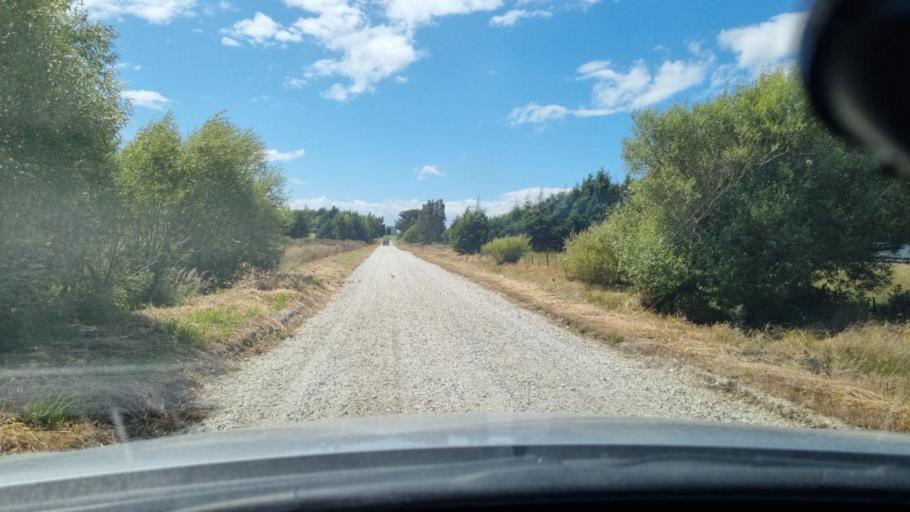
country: NZ
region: Southland
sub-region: Invercargill City
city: Invercargill
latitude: -46.4354
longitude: 168.3896
